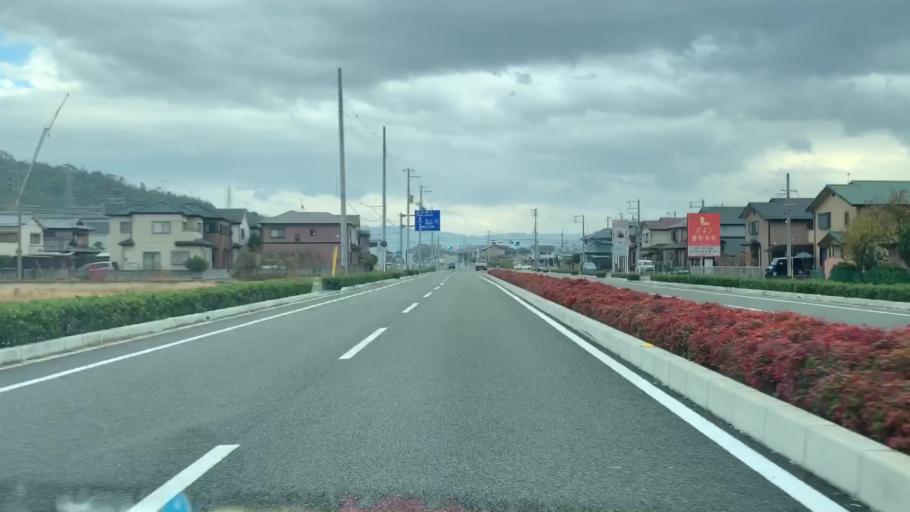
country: JP
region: Wakayama
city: Wakayama-shi
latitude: 34.2183
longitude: 135.2074
